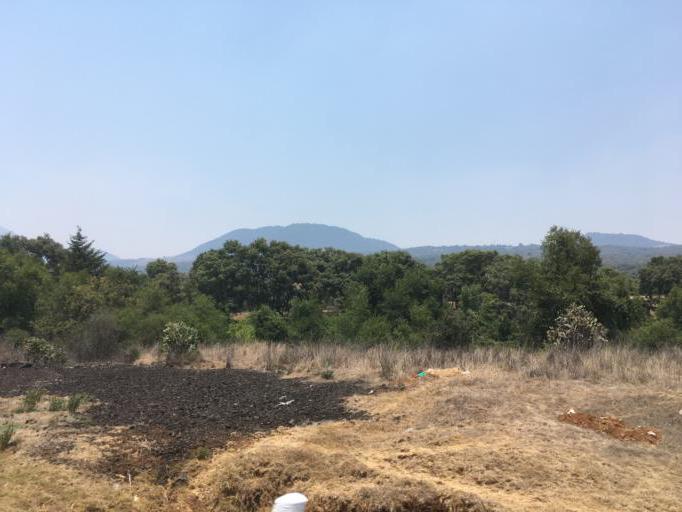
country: MX
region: Michoacan
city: Quiroga
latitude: 19.6395
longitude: -101.4847
